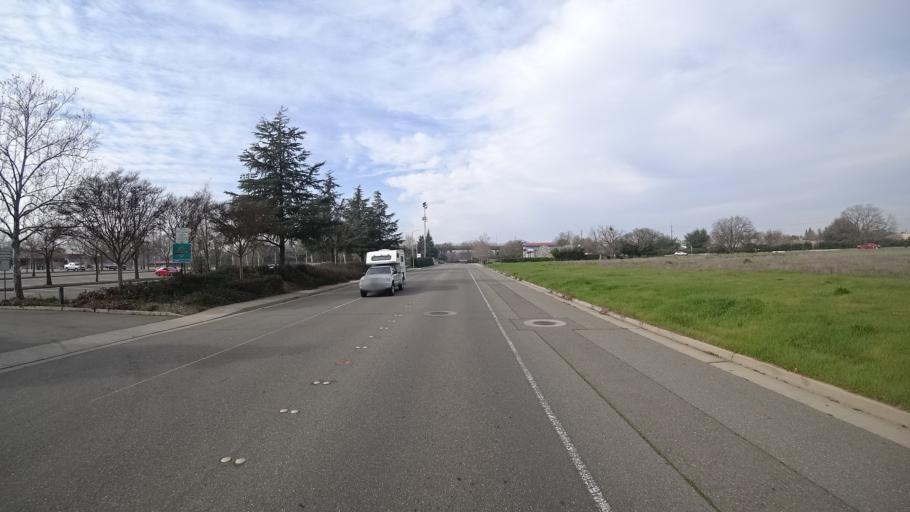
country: US
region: California
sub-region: Yolo County
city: Davis
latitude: 38.5451
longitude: -121.7231
